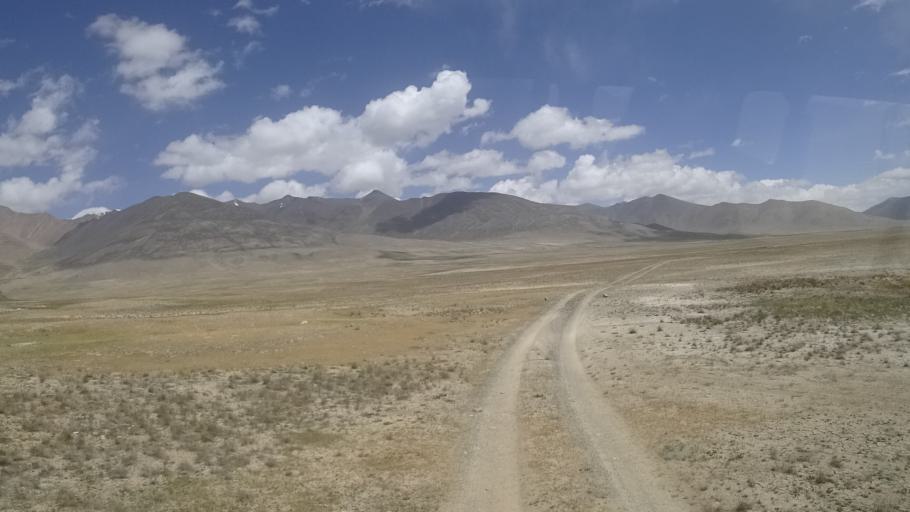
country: TJ
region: Gorno-Badakhshan
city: Murghob
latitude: 37.4748
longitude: 73.9724
